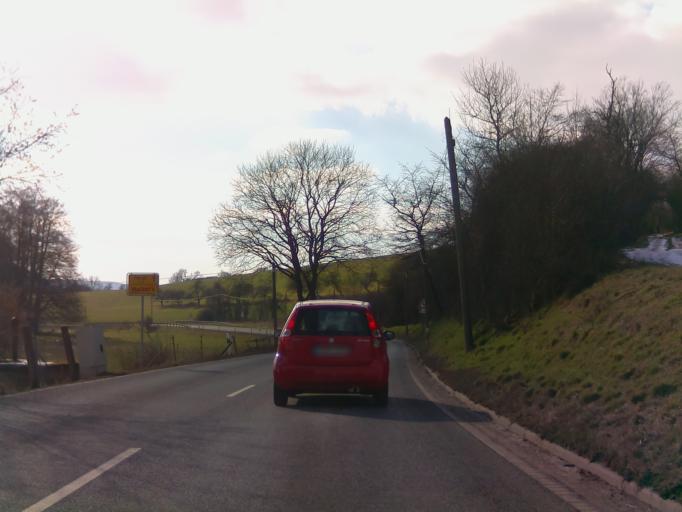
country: DE
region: Thuringia
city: Rippershausen
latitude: 50.5998
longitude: 10.3699
